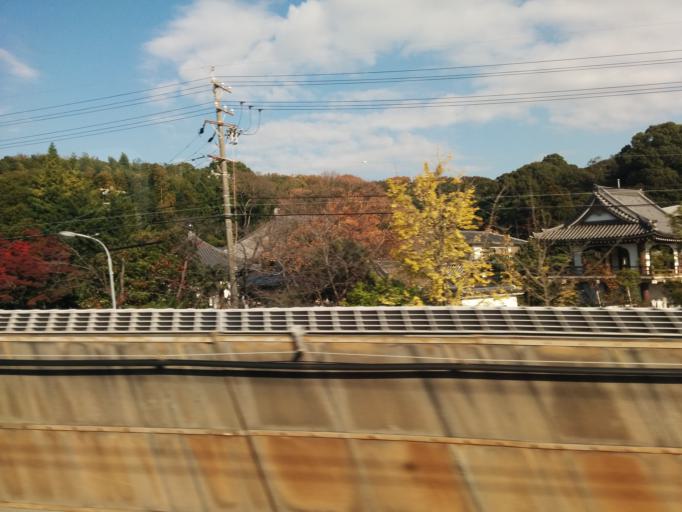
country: JP
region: Aichi
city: Obu
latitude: 35.0676
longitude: 136.9415
